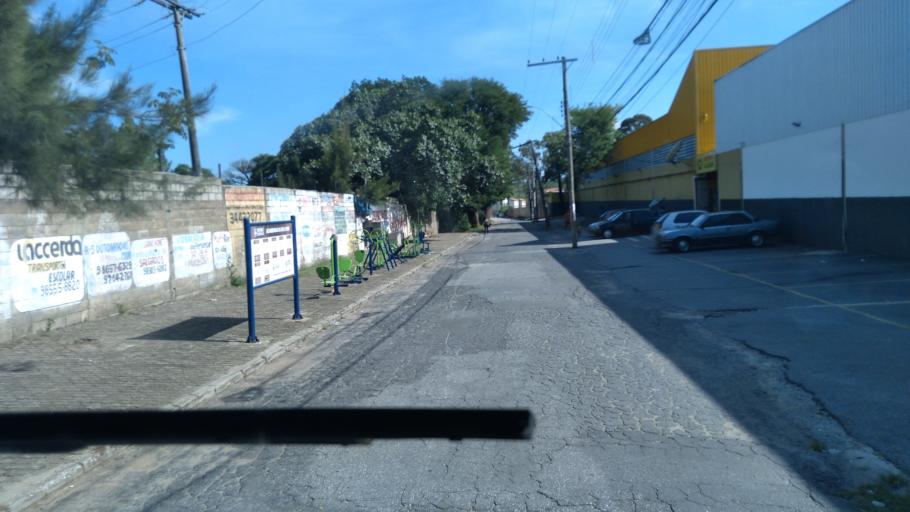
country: BR
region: Minas Gerais
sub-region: Santa Luzia
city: Santa Luzia
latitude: -19.8456
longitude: -43.8845
